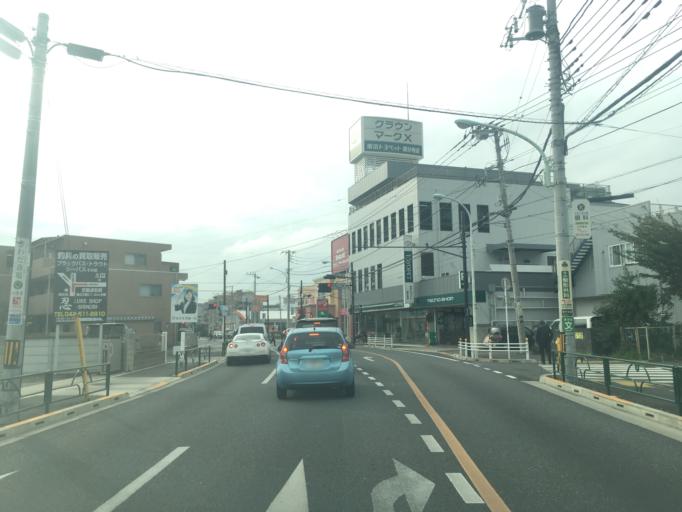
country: JP
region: Tokyo
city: Kokubunji
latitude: 35.7131
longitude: 139.4670
